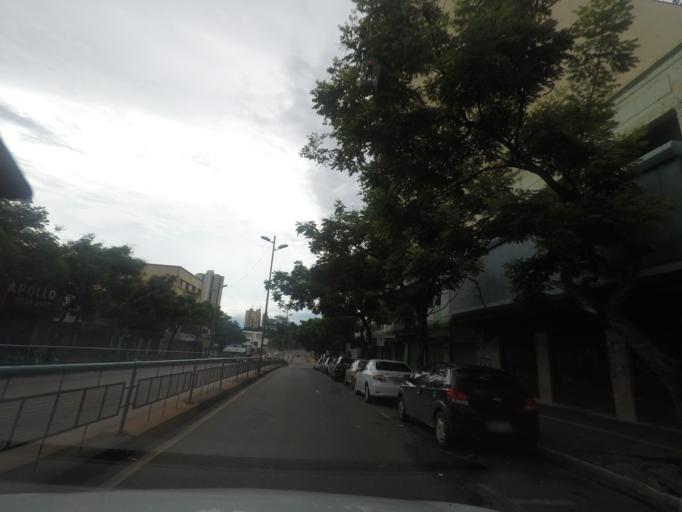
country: BR
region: Goias
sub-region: Goiania
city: Goiania
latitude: -16.6731
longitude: -49.2518
